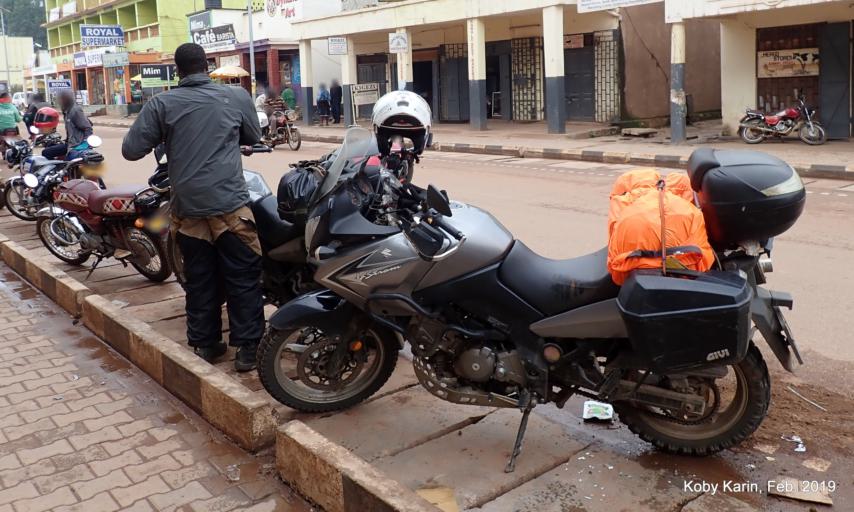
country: UG
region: Western Region
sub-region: Kabale District
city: Kabale
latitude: -1.2528
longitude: 29.9874
